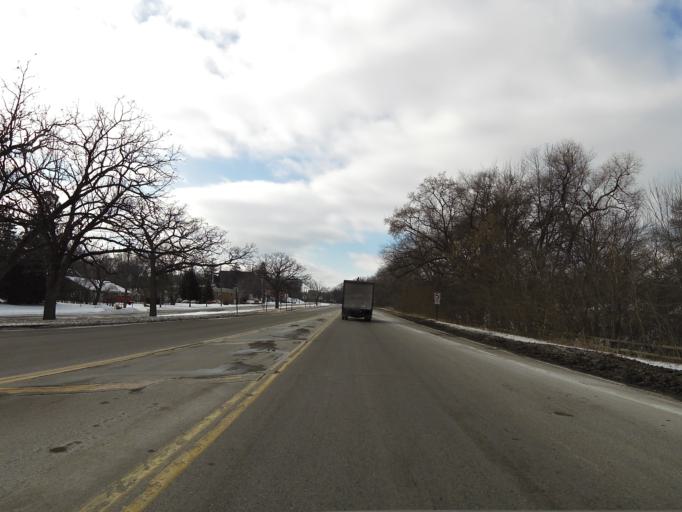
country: US
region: Minnesota
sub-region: Hennepin County
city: Minnetonka Mills
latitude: 44.9209
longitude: -93.4288
